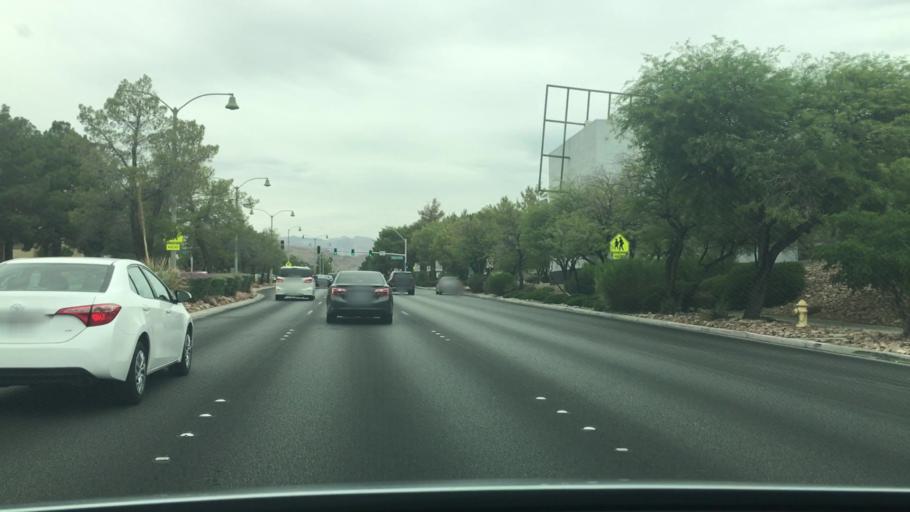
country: US
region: Nevada
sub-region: Clark County
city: Summerlin South
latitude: 36.1445
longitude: -115.3048
